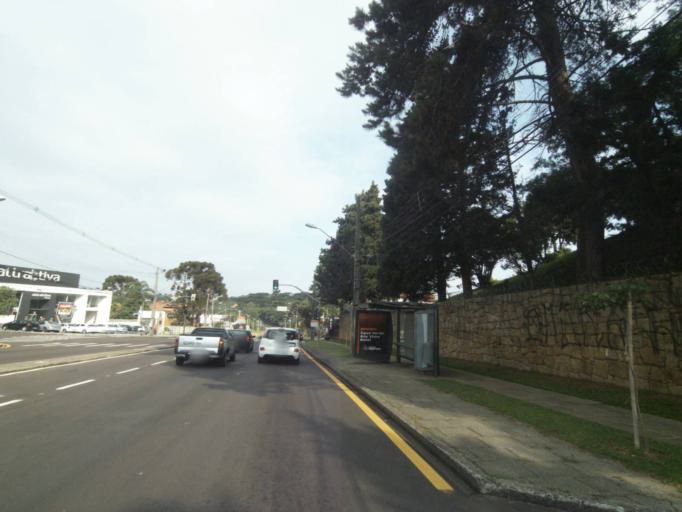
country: BR
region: Parana
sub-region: Curitiba
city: Curitiba
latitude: -25.4140
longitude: -49.3111
